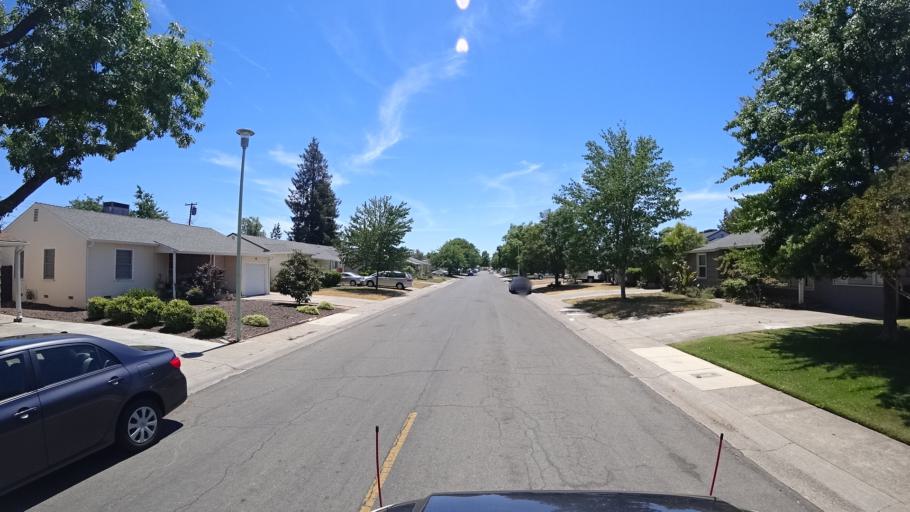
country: US
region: California
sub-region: Sacramento County
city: Parkway
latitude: 38.5244
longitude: -121.4919
